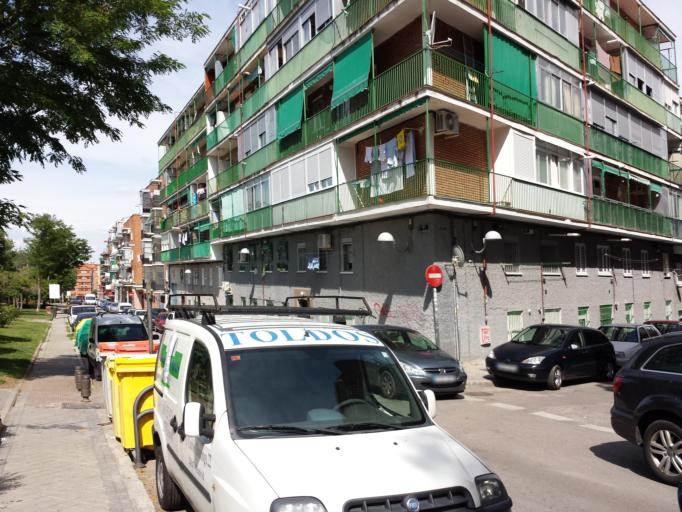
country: ES
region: Madrid
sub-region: Provincia de Madrid
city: Latina
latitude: 40.3912
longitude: -3.7465
